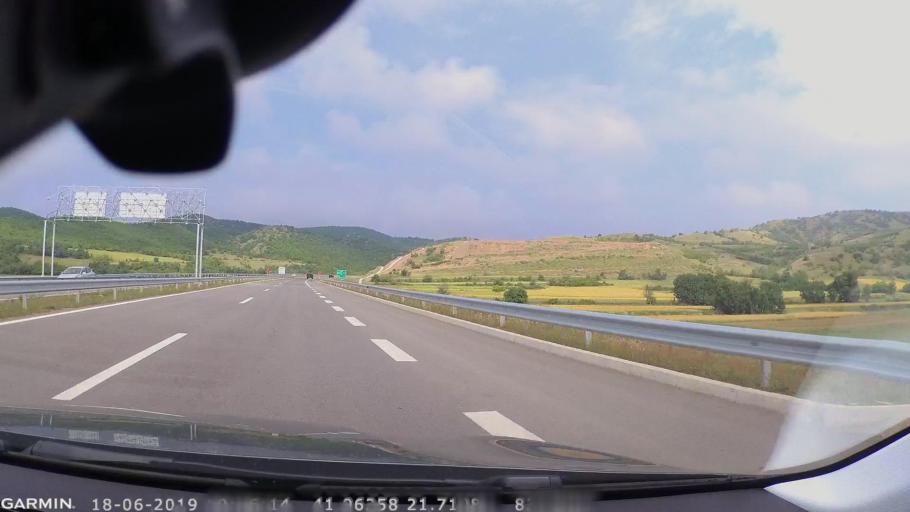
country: MK
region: Petrovec
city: Sredno Konjare
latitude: 41.9470
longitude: 21.8024
